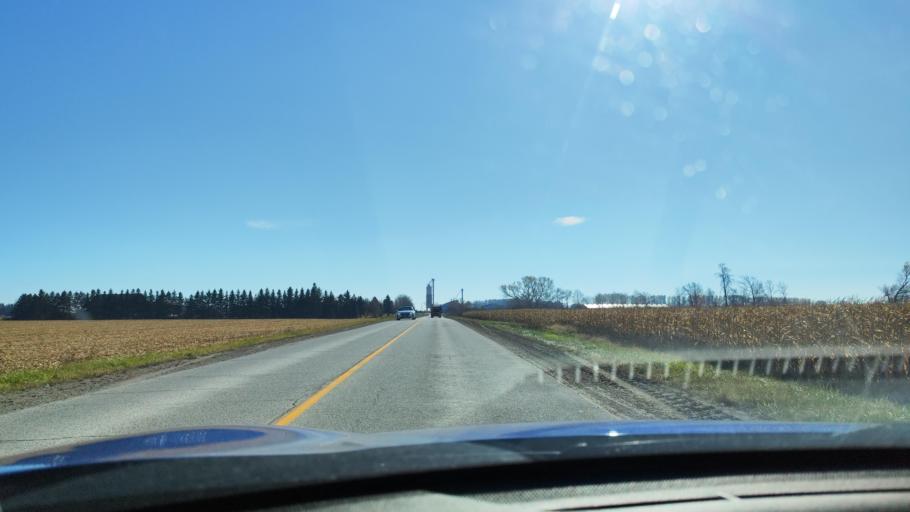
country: CA
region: Ontario
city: Wasaga Beach
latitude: 44.4448
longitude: -79.9996
